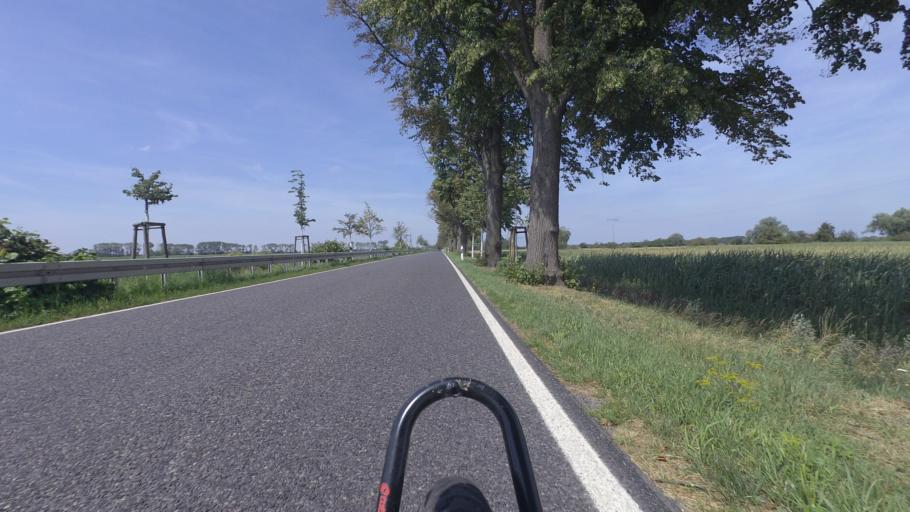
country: DE
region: Brandenburg
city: Rhinow
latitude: 52.7625
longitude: 12.2918
